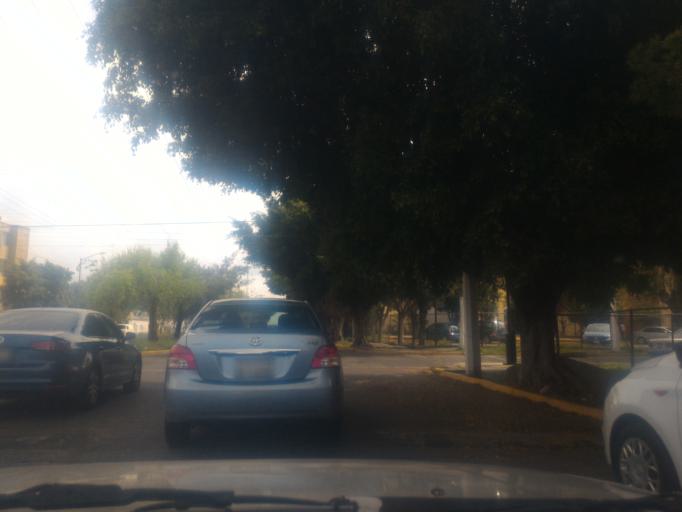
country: MX
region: Jalisco
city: Guadalajara
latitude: 20.6712
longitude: -103.4178
